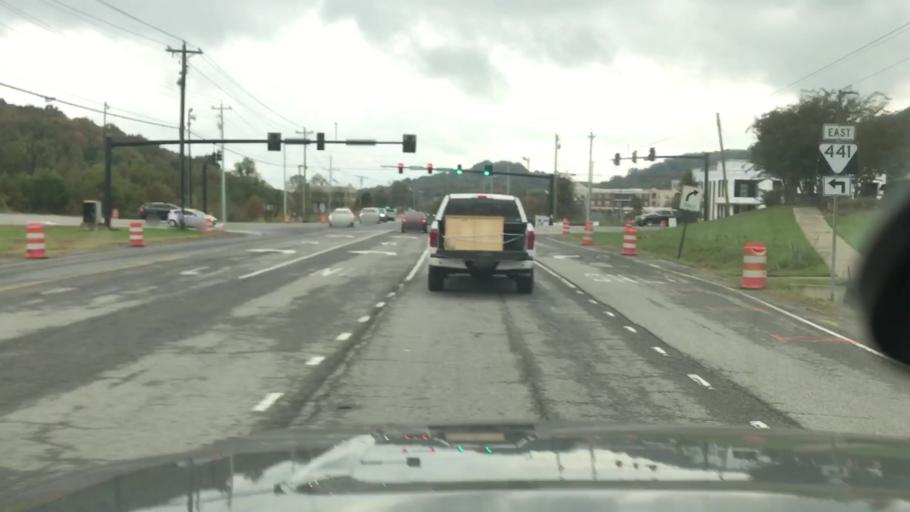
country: US
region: Tennessee
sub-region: Williamson County
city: Franklin
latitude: 35.9739
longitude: -86.8326
